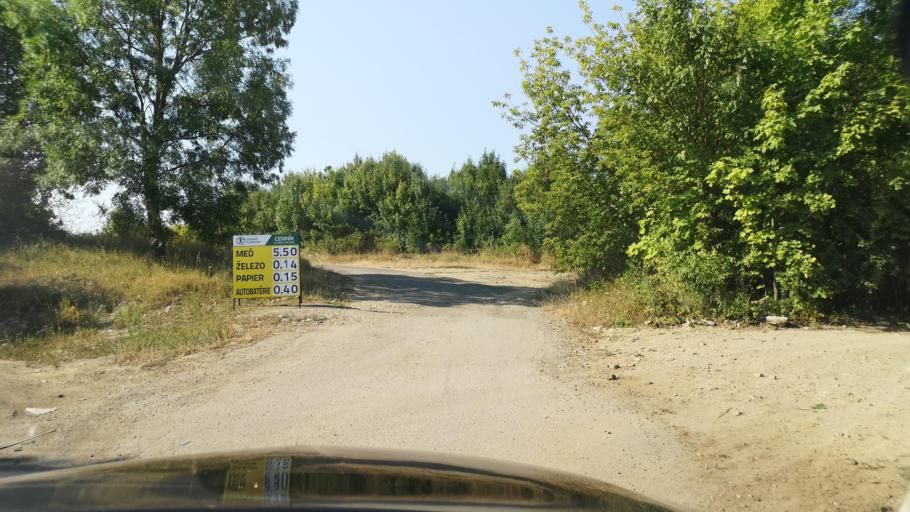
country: SK
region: Nitriansky
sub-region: Okres Nitra
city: Nitra
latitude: 48.3147
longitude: 18.0432
